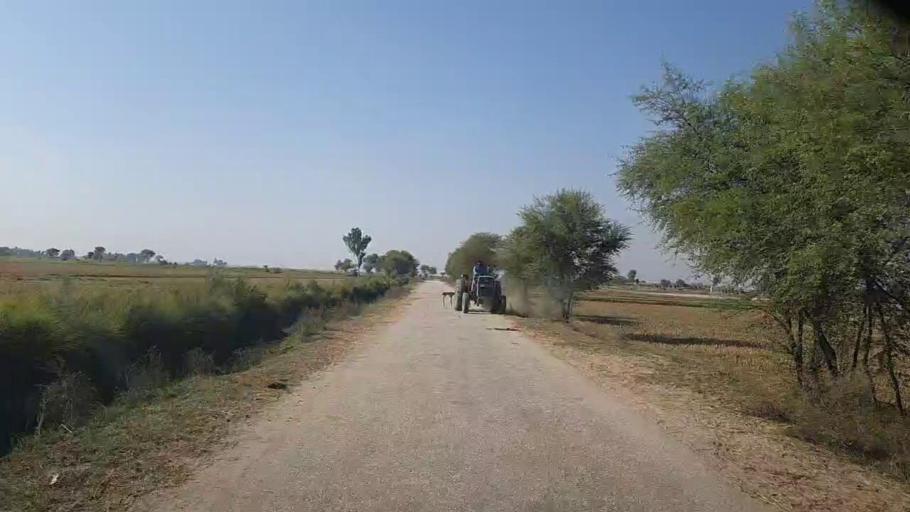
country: PK
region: Sindh
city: Tangwani
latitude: 28.2462
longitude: 68.9480
